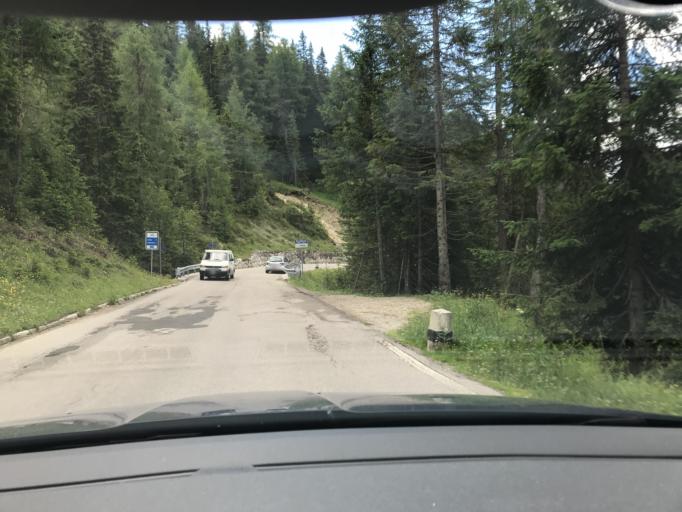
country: IT
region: Veneto
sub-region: Provincia di Belluno
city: Livinallongo del Col di Lana
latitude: 46.5055
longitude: 11.9973
